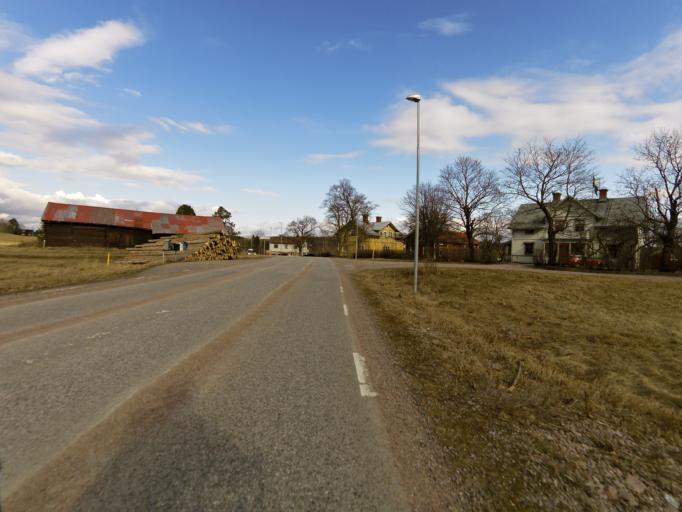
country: SE
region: Dalarna
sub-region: Avesta Kommun
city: Horndal
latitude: 60.4515
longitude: 16.4504
